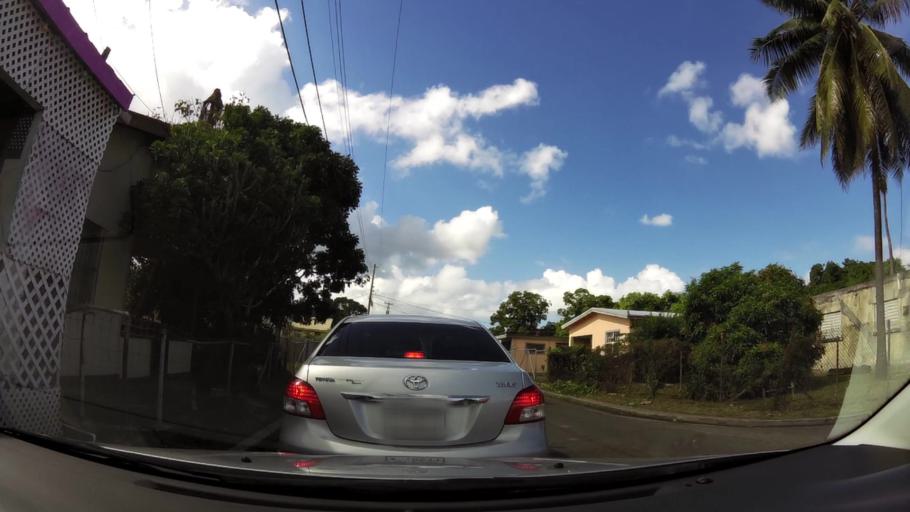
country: AG
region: Saint John
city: Saint John's
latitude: 17.1068
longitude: -61.8411
